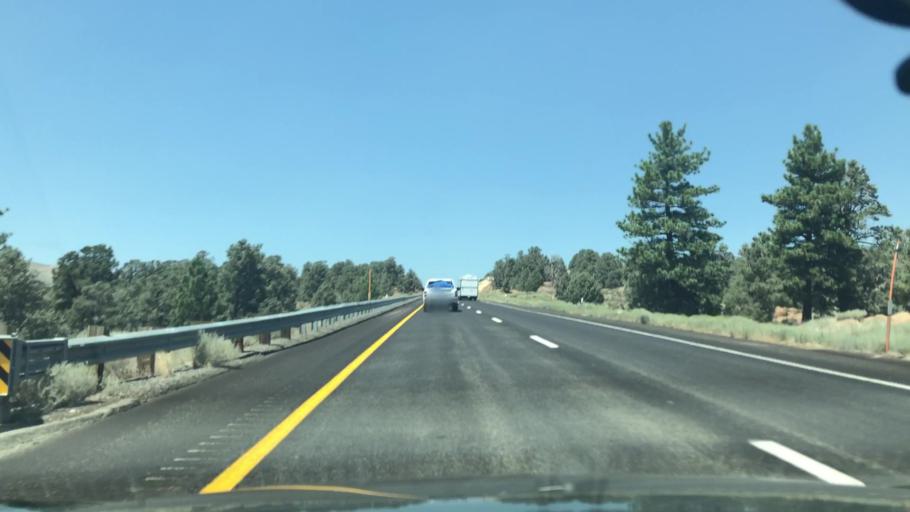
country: US
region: California
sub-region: Inyo County
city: West Bishop
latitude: 37.5256
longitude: -118.6221
